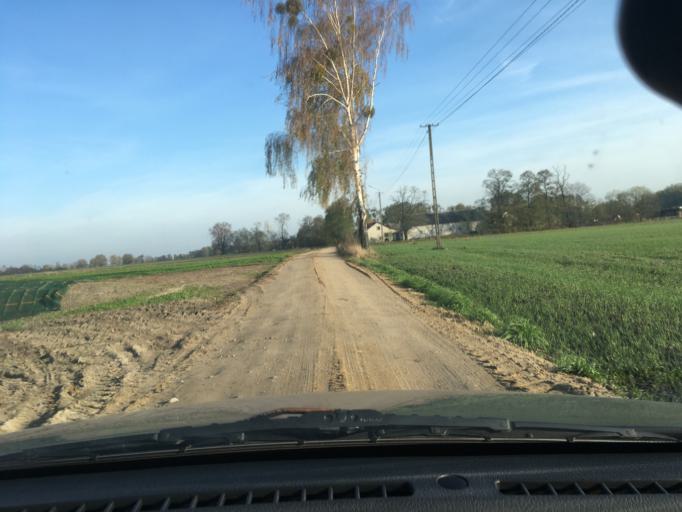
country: PL
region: Masovian Voivodeship
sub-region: Powiat plocki
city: Mala Wies
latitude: 52.4429
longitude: 20.1082
